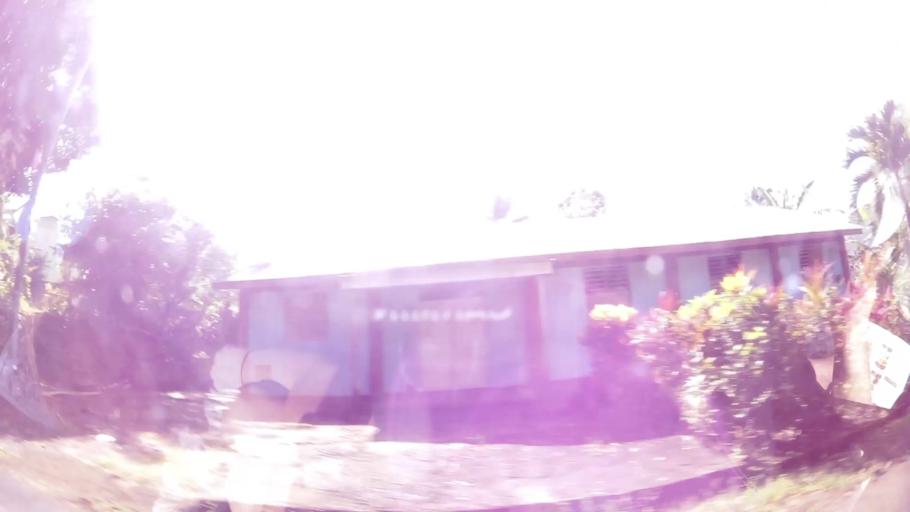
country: DM
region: Saint David
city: Castle Bruce
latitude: 15.4780
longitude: -61.2512
